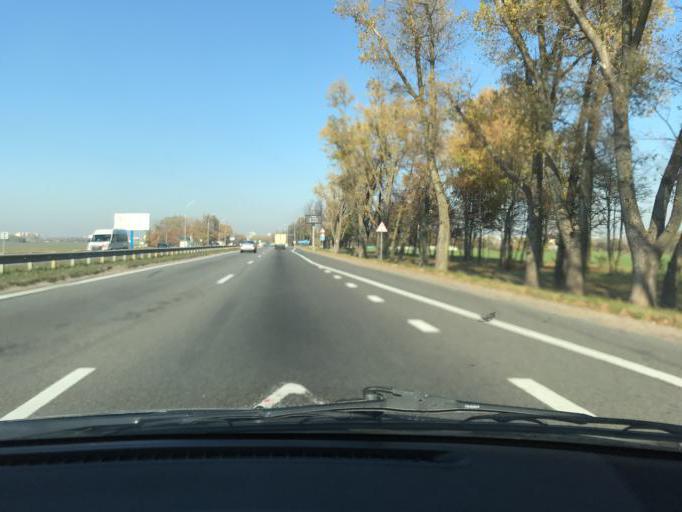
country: BY
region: Minsk
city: Yubilyeyny
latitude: 53.8017
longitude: 27.5296
